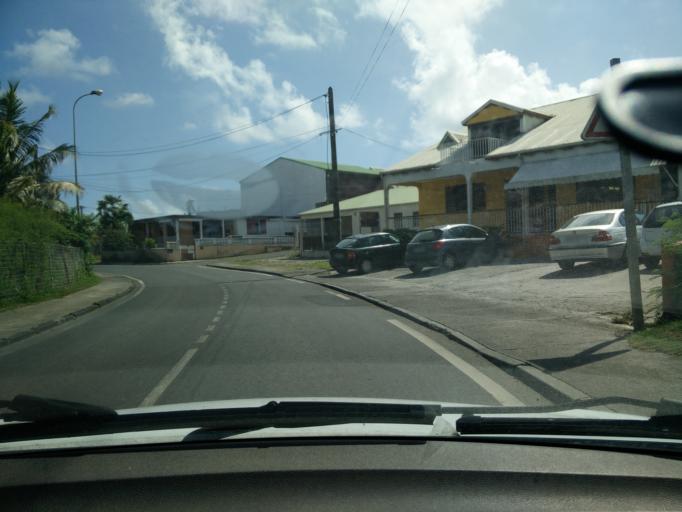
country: GP
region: Guadeloupe
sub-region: Guadeloupe
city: Le Moule
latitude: 16.3284
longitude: -61.3521
